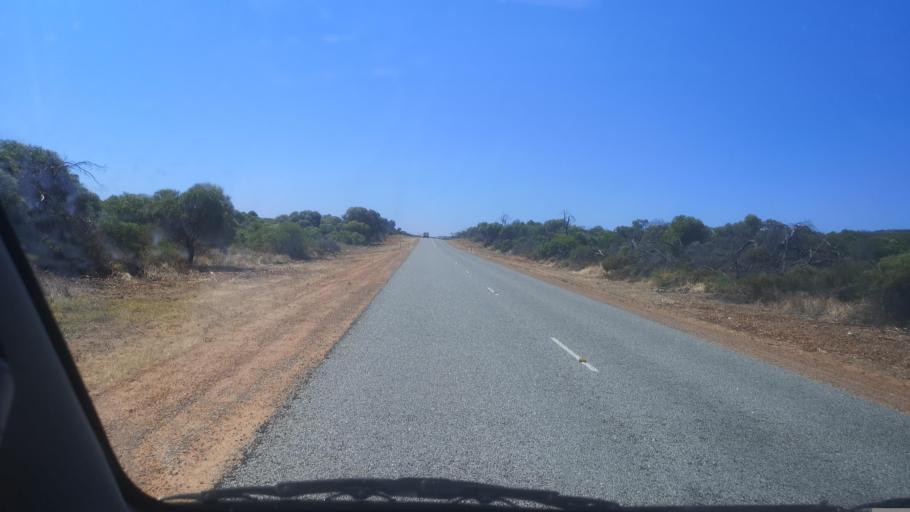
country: AU
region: Western Australia
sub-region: Northampton Shire
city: Kalbarri
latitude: -28.0689
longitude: 114.1954
